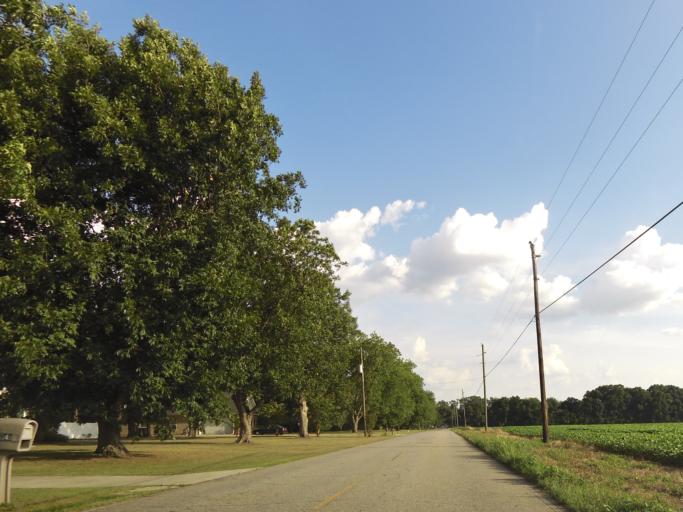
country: US
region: Georgia
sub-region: Houston County
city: Centerville
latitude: 32.7123
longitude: -83.6792
